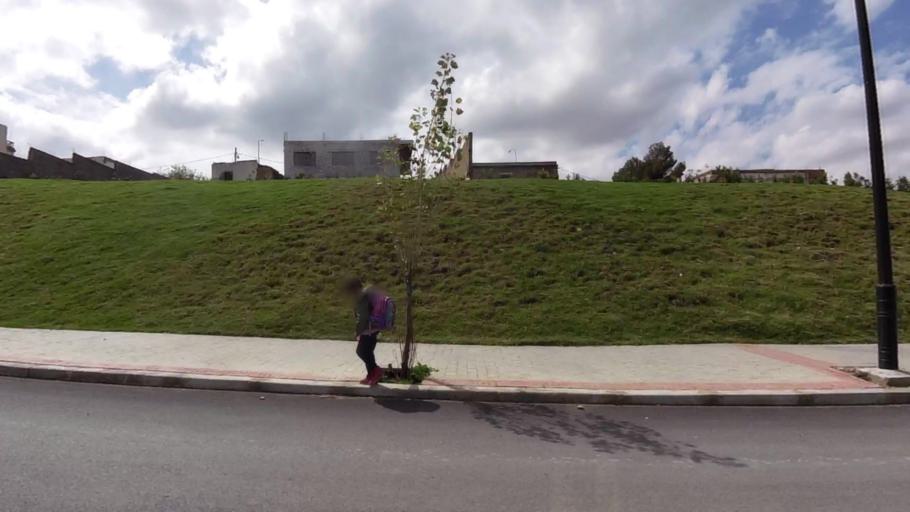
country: MA
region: Tanger-Tetouan
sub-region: Tanger-Assilah
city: Tangier
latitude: 35.7767
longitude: -5.7522
